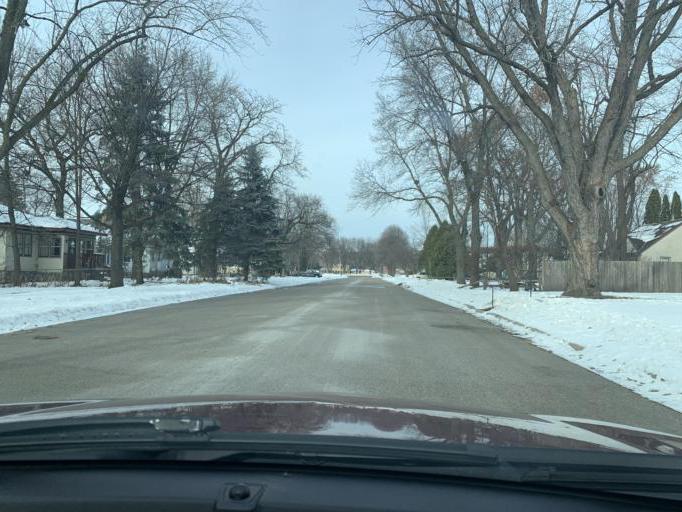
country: US
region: Minnesota
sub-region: Washington County
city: Saint Paul Park
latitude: 44.8389
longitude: -92.9870
